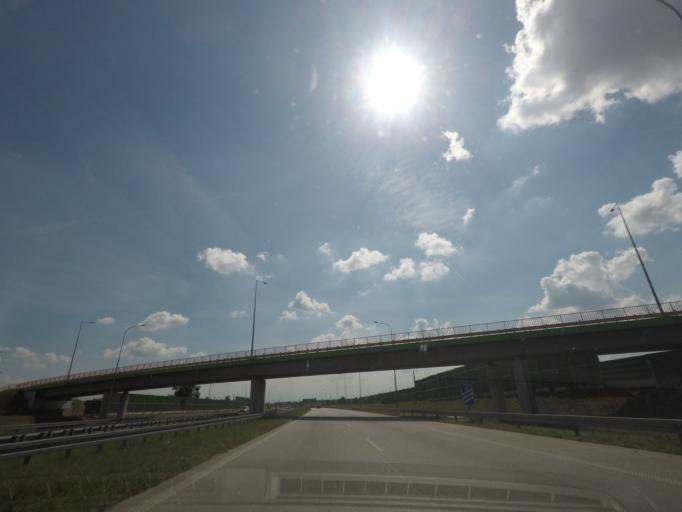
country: PL
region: Lodz Voivodeship
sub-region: Powiat lodzki wschodni
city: Andrespol
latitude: 51.8041
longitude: 19.6255
